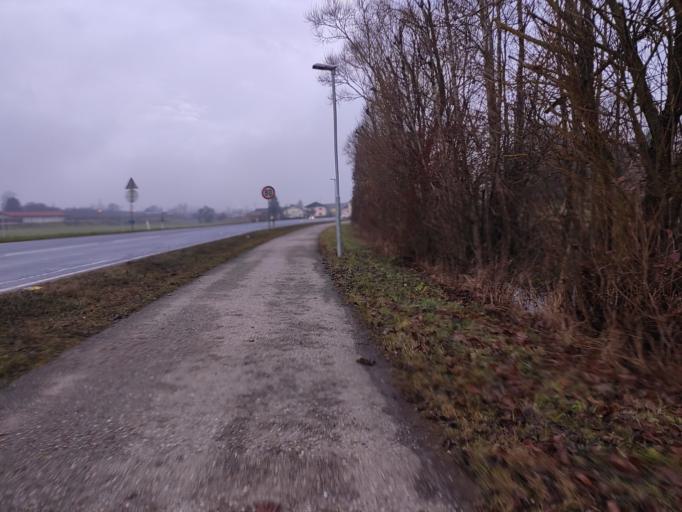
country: AT
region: Salzburg
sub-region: Politischer Bezirk Salzburg-Umgebung
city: Strasswalchen
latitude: 47.9710
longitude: 13.2722
